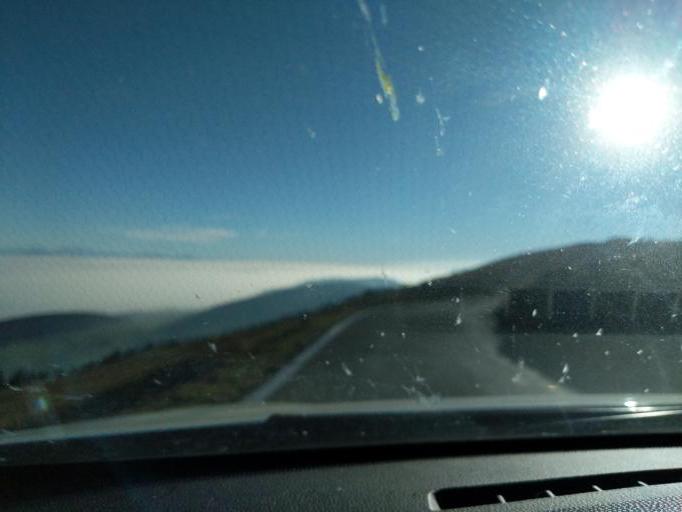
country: CH
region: Bern
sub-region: Jura bernois
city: Saint-Imier
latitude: 47.1243
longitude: 7.0405
